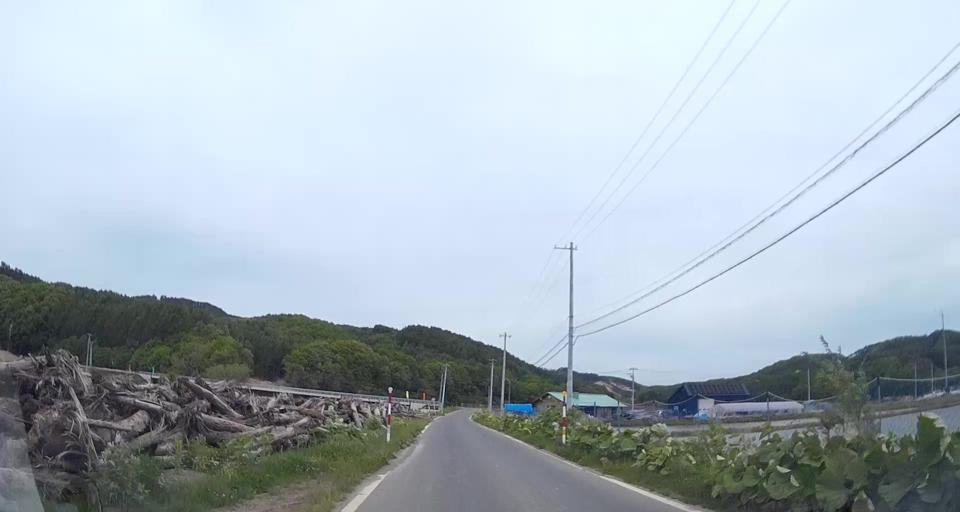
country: JP
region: Hokkaido
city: Chitose
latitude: 42.7549
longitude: 141.9719
